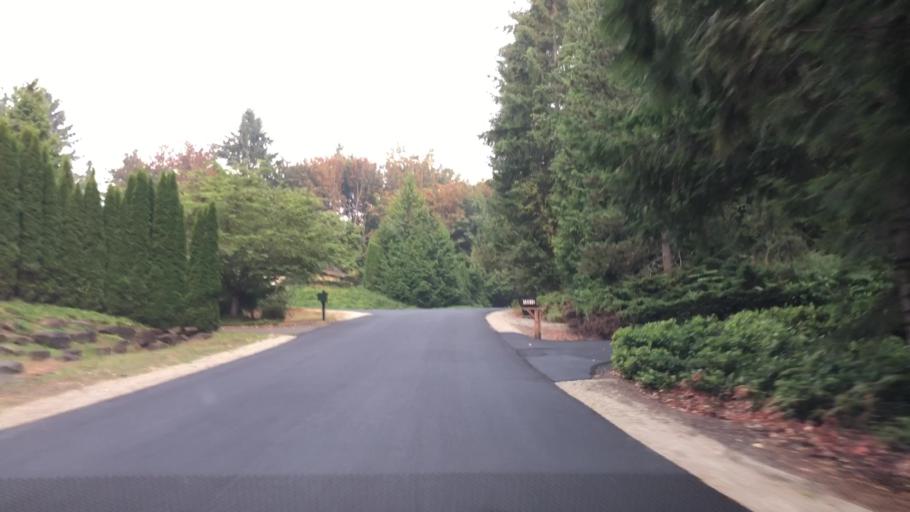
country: US
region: Washington
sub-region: King County
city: Cottage Lake
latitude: 47.7300
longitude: -122.0994
